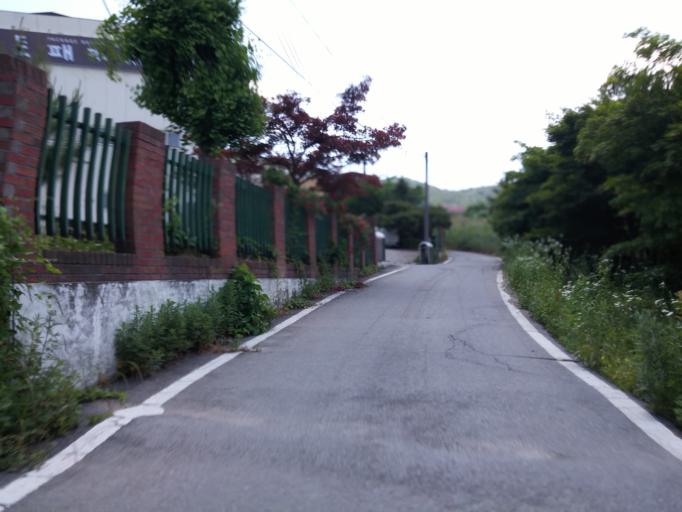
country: KR
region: Chungcheongbuk-do
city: Cheongju-si
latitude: 36.5568
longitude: 127.4350
